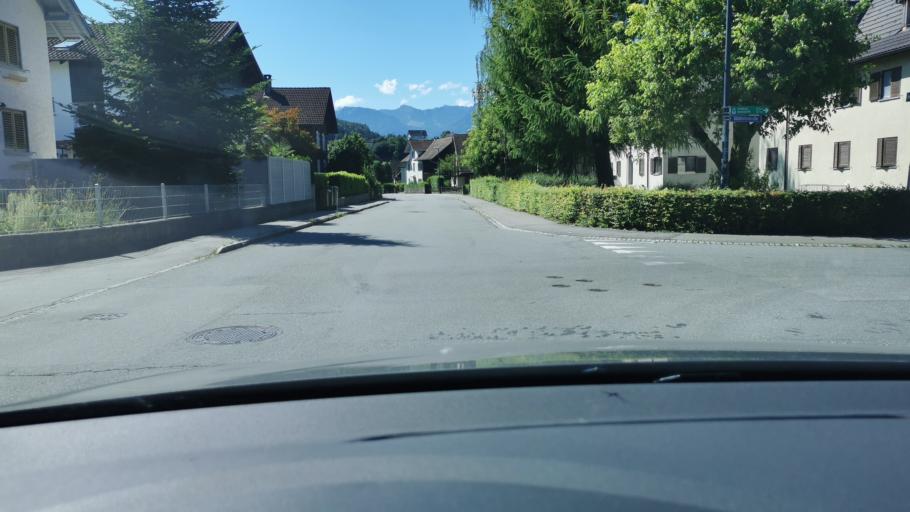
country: AT
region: Vorarlberg
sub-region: Politischer Bezirk Feldkirch
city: Rankweil
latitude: 47.2756
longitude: 9.6449
